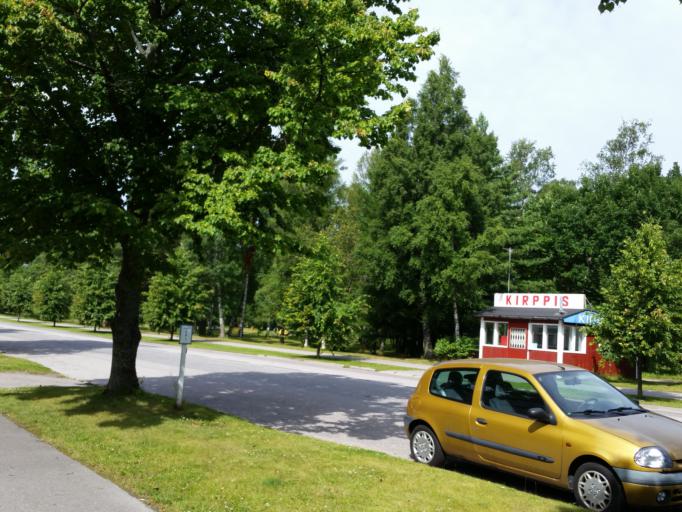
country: FI
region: Uusimaa
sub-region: Raaseporin
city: Hanko
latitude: 59.8284
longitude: 22.9613
